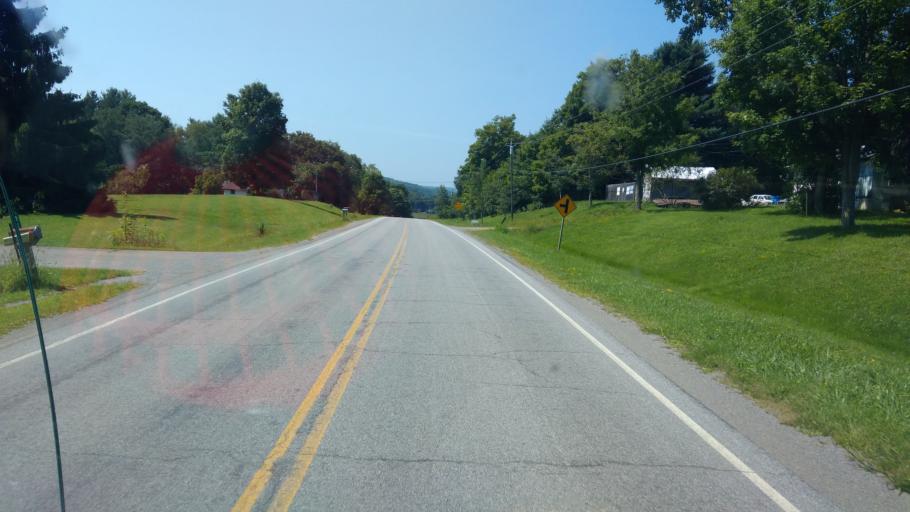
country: US
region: New York
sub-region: Allegany County
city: Belmont
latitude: 42.3027
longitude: -77.9846
